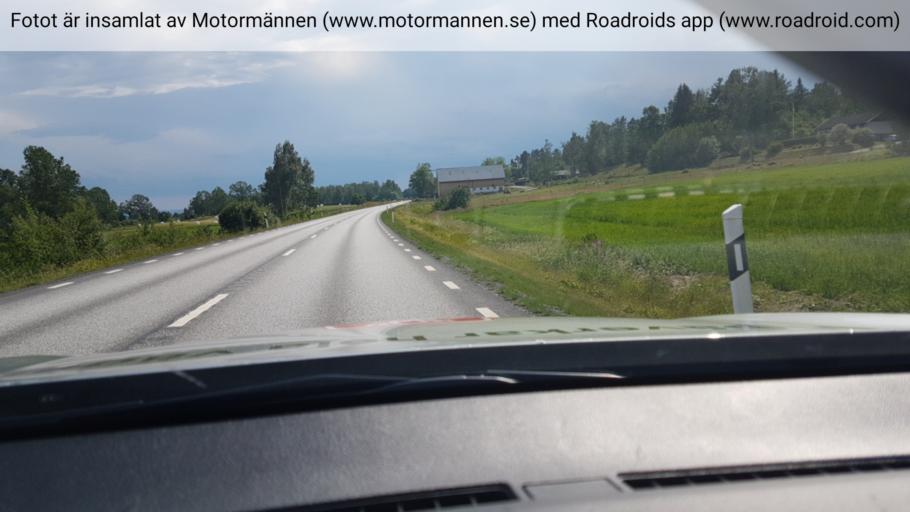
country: SE
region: Joenkoeping
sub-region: Habo Kommun
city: Habo
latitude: 58.0625
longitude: 14.1947
